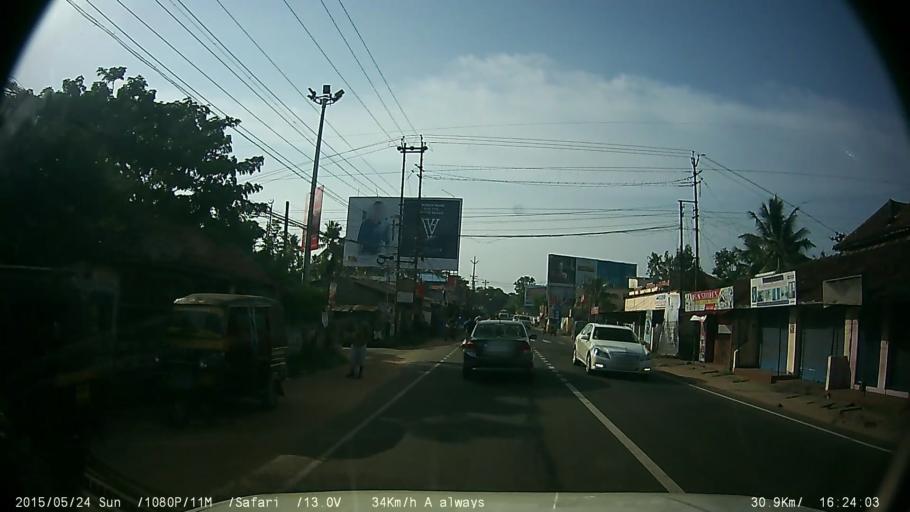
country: IN
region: Kerala
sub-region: Alappuzha
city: Alleppey
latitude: 9.5045
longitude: 76.3284
